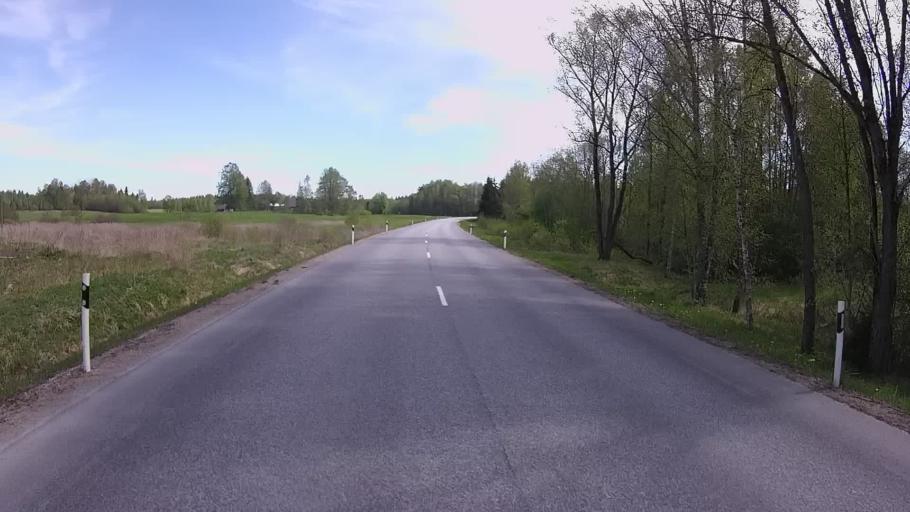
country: EE
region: Valgamaa
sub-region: Valga linn
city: Valga
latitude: 57.7108
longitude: 26.2280
